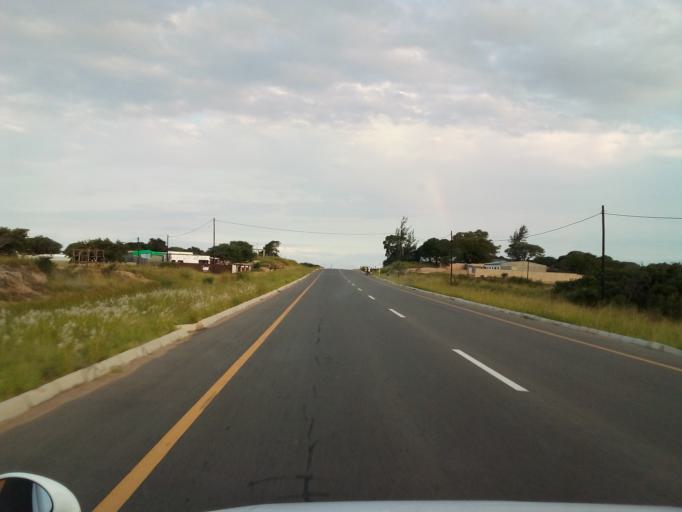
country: MZ
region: Maputo City
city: Maputo
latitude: -26.0509
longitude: 32.5794
